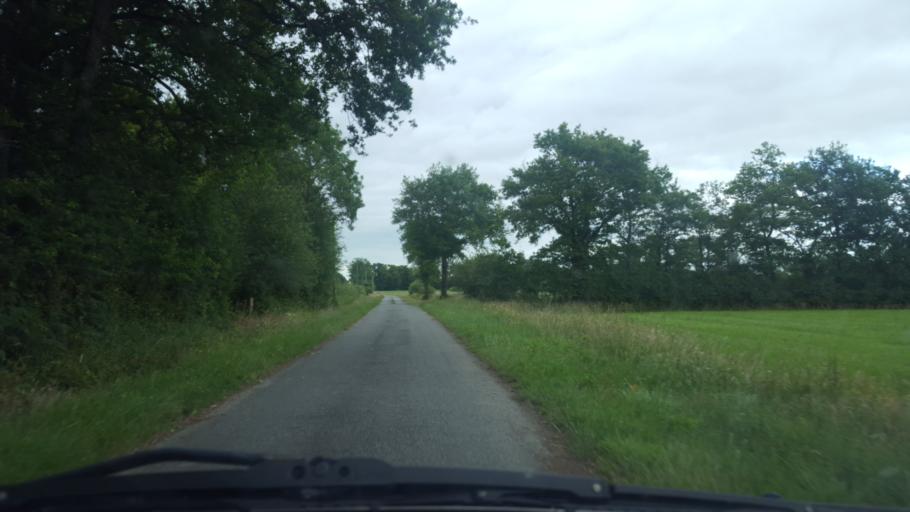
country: FR
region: Pays de la Loire
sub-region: Departement de la Loire-Atlantique
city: Saint-Philbert-de-Grand-Lieu
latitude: 47.0123
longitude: -1.6826
